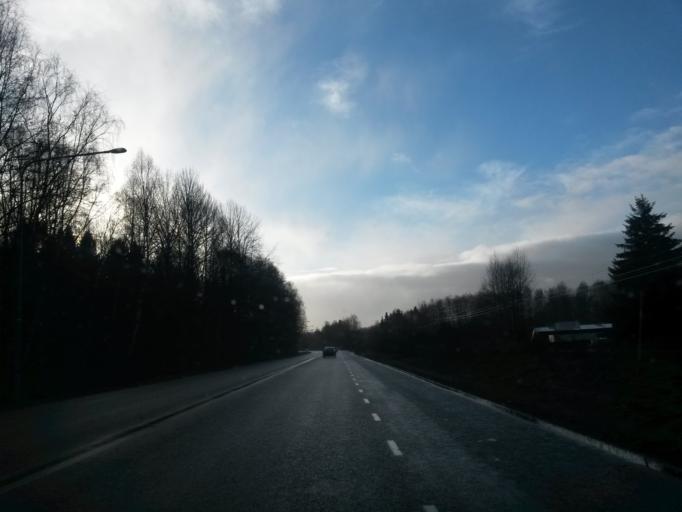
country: SE
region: Vaestra Goetaland
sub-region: Boras Kommun
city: Boras
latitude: 57.7755
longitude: 12.9795
